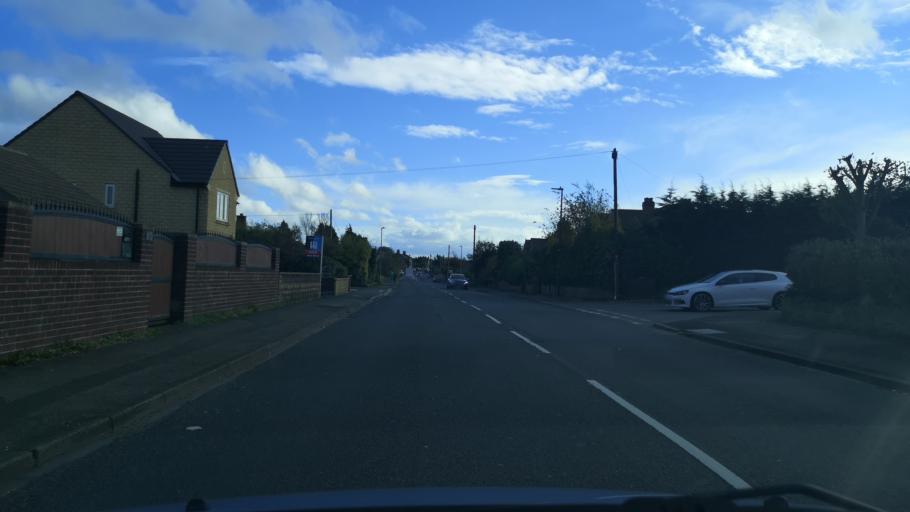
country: GB
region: England
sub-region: Kirklees
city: Heckmondwike
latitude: 53.7170
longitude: -1.6627
